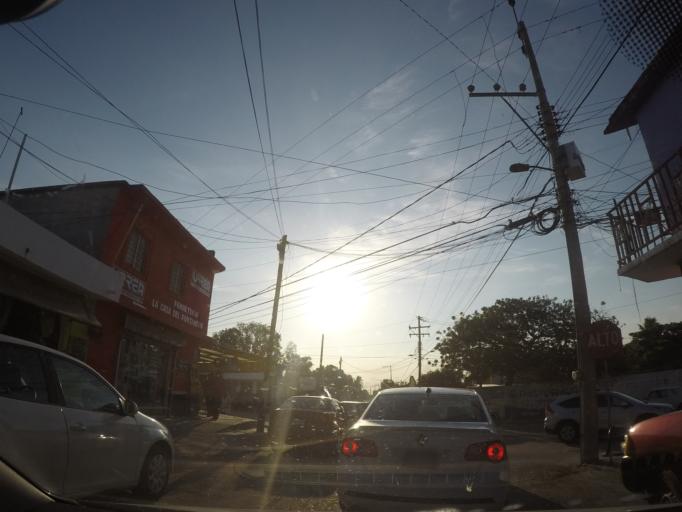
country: MX
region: Oaxaca
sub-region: Salina Cruz
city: Salina Cruz
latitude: 16.2036
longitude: -95.1985
